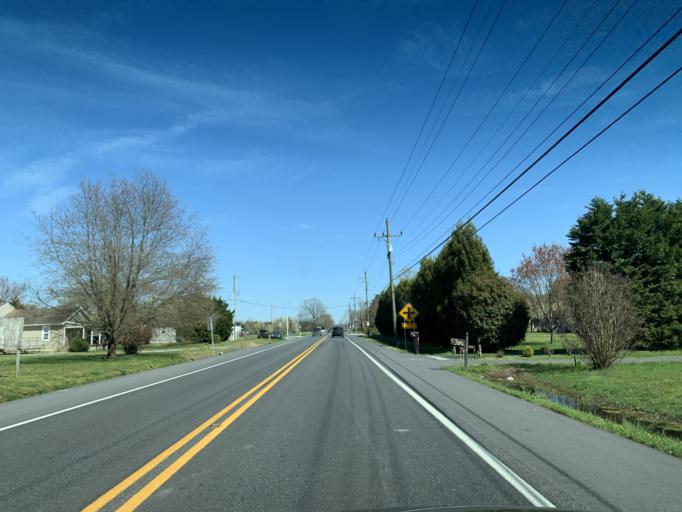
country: US
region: Delaware
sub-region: Kent County
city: Harrington
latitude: 38.9277
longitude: -75.5186
